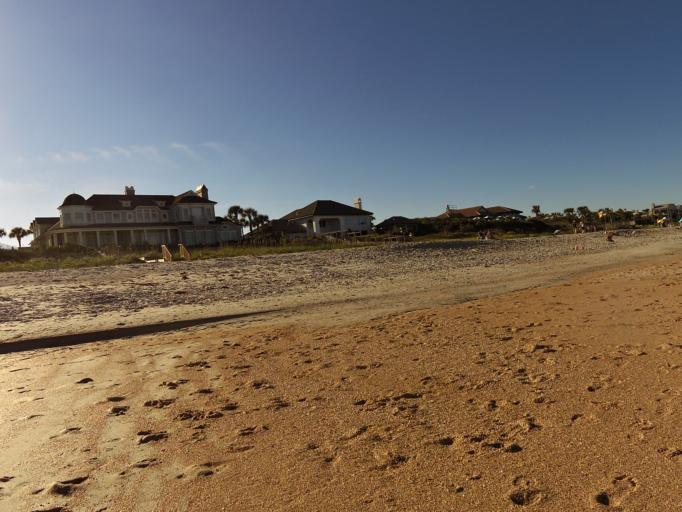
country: US
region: Florida
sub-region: Saint Johns County
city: Sawgrass
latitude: 30.1915
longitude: -81.3633
